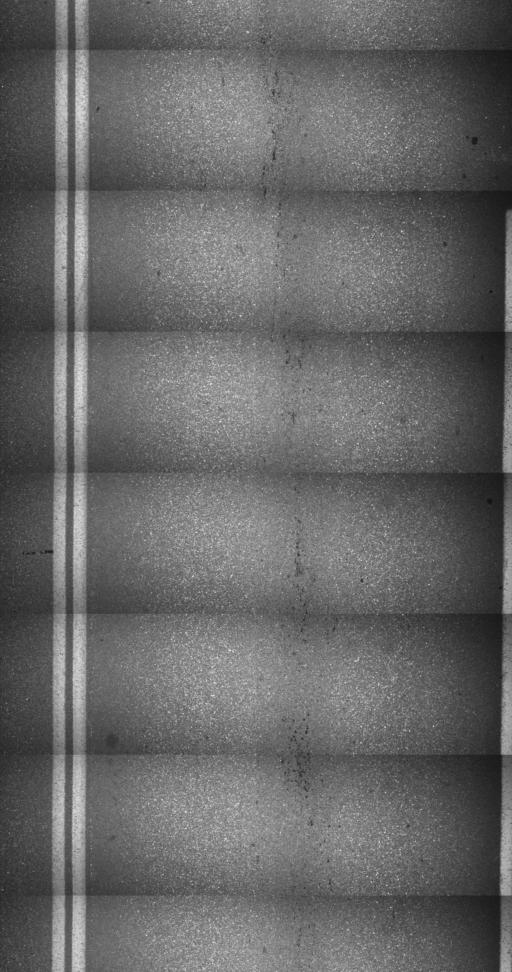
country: US
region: New Hampshire
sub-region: Grafton County
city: Orford
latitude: 43.9301
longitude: -72.1213
